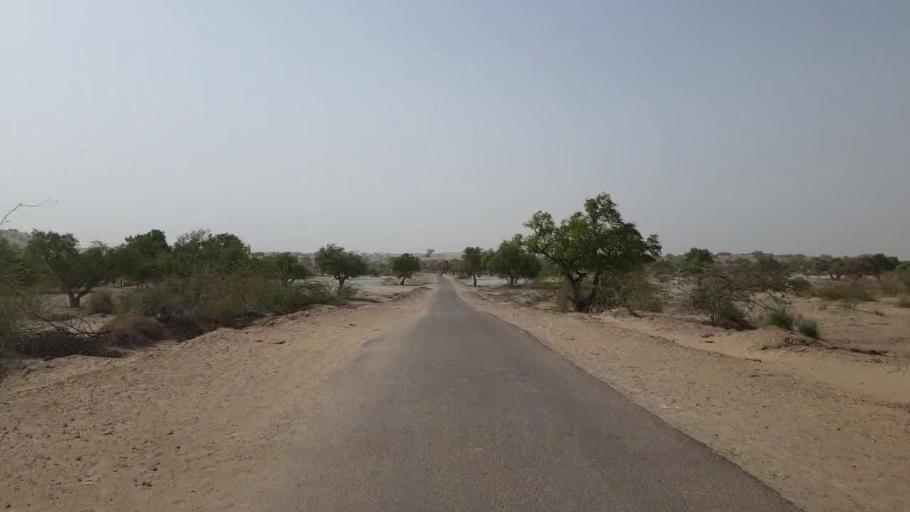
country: PK
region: Sindh
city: Mithi
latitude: 24.6144
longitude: 69.9198
